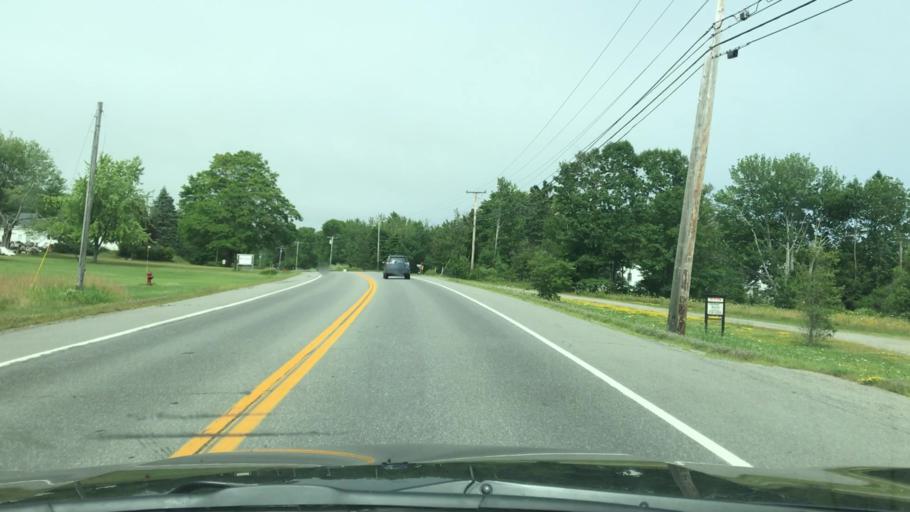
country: US
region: Maine
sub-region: Waldo County
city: Belfast
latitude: 44.4375
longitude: -68.9402
